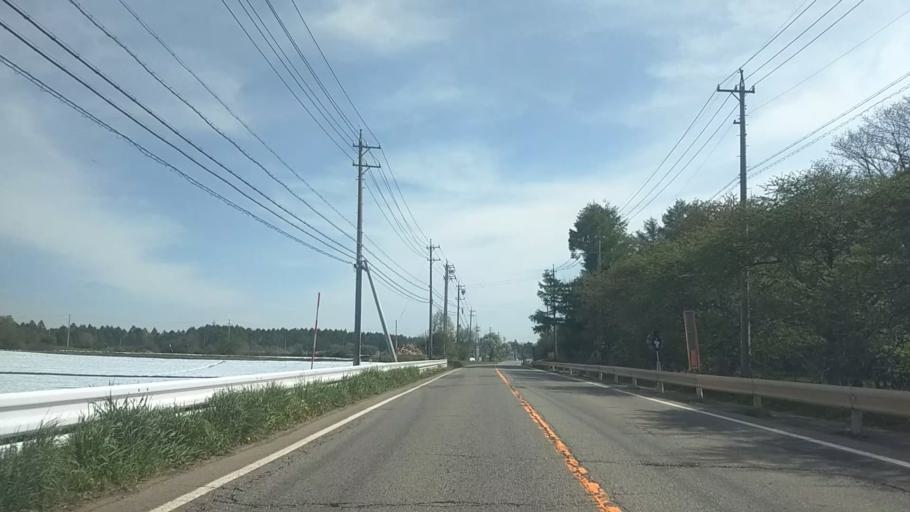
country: JP
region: Nagano
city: Saku
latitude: 35.9660
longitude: 138.4769
